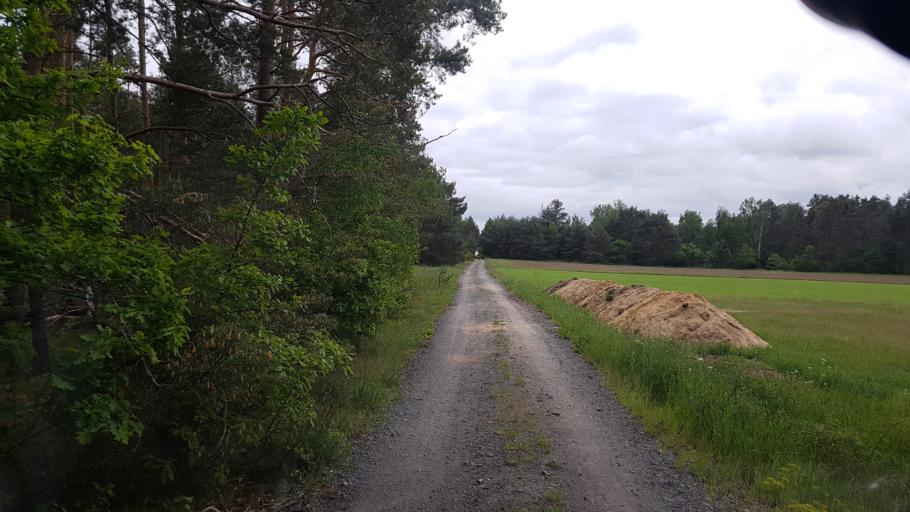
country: DE
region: Brandenburg
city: Elsterwerda
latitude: 51.5016
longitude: 13.5035
